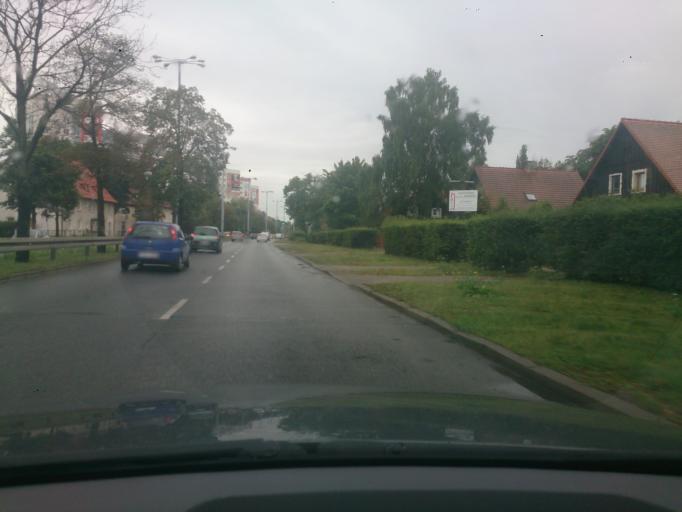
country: PL
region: Pomeranian Voivodeship
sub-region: Sopot
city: Sopot
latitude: 54.4226
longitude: 18.5642
